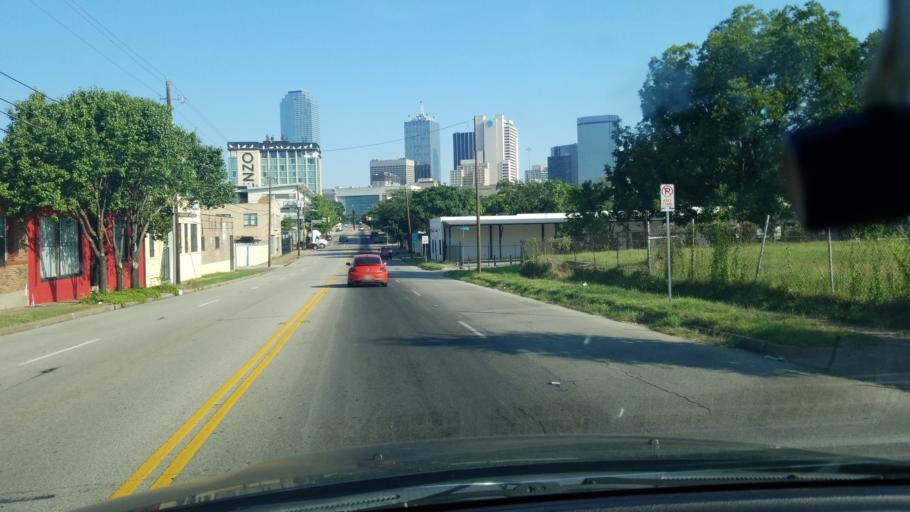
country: US
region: Texas
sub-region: Dallas County
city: Dallas
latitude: 32.7707
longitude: -96.7929
